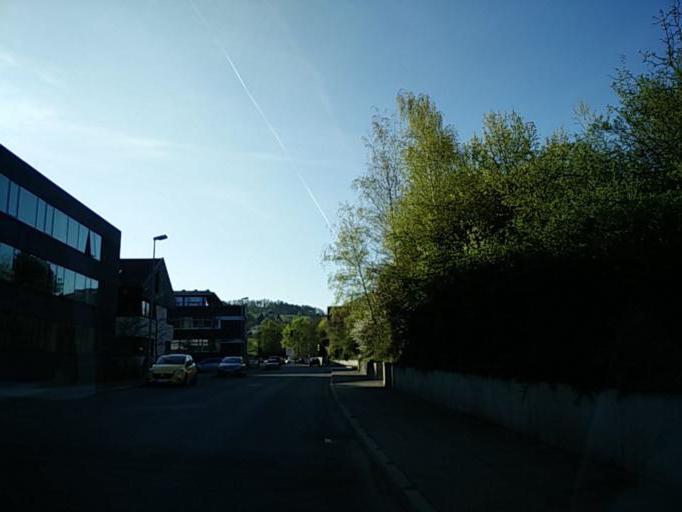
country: DE
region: Baden-Wuerttemberg
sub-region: Tuebingen Region
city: Tuebingen
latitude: 48.5254
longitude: 9.0267
